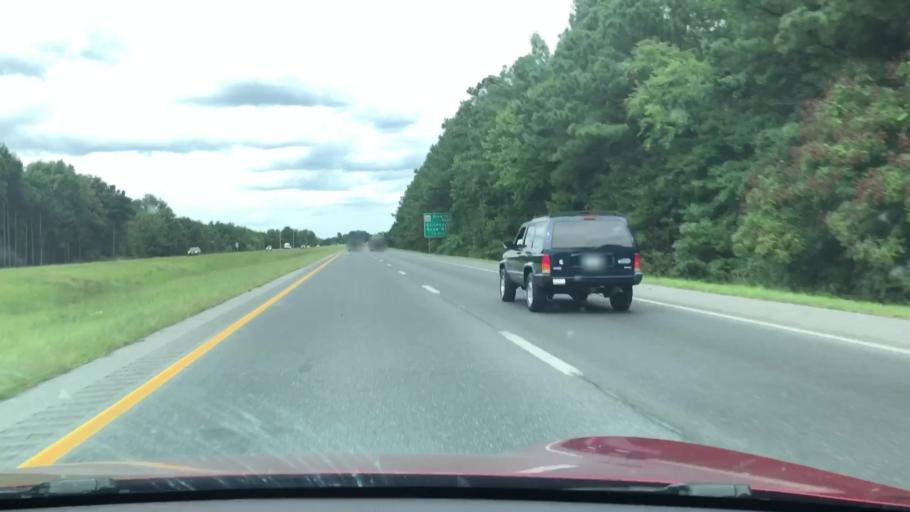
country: US
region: Maryland
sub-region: Wicomico County
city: Salisbury
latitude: 38.3271
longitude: -75.5777
